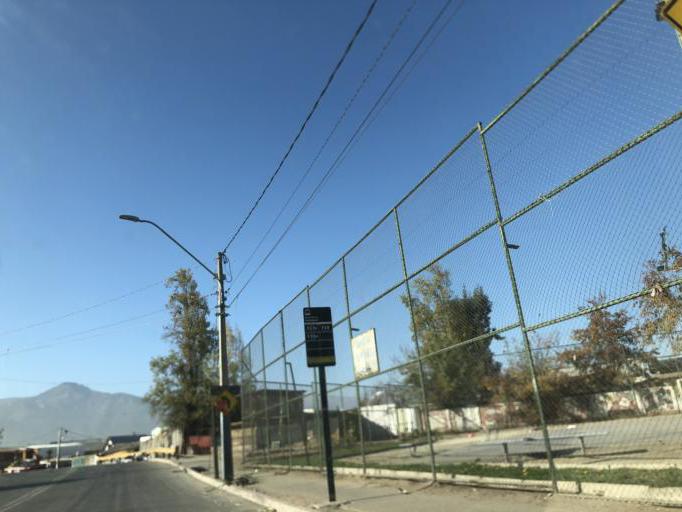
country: CL
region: Santiago Metropolitan
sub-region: Provincia de Cordillera
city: Puente Alto
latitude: -33.6163
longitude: -70.5935
